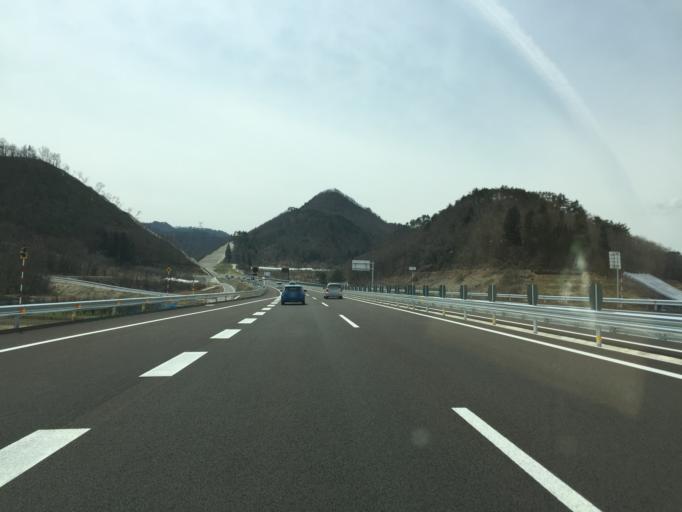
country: JP
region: Yamagata
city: Kaminoyama
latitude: 38.1254
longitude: 140.2543
